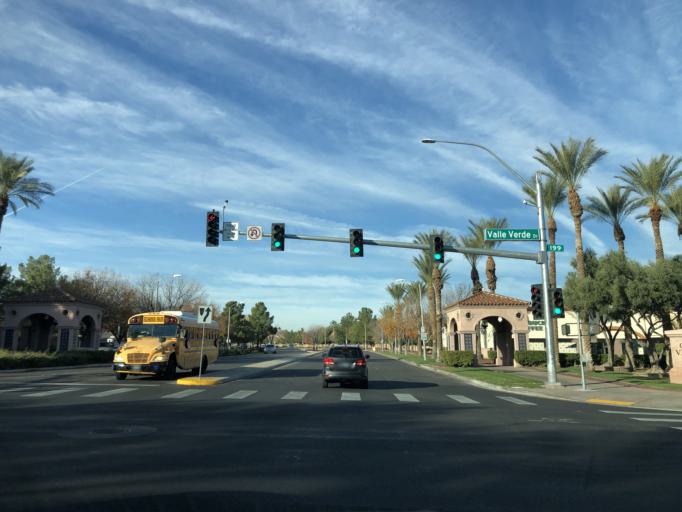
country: US
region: Nevada
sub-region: Clark County
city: Whitney
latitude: 36.0238
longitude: -115.0622
